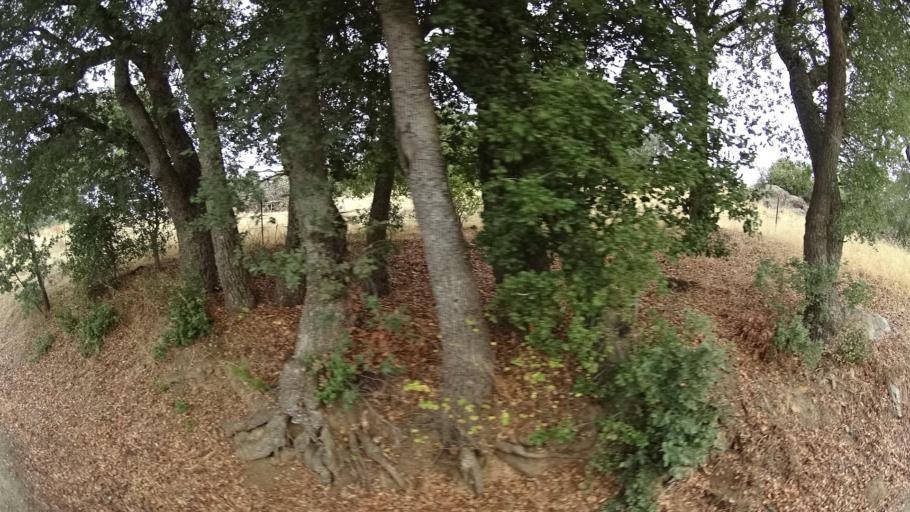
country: US
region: California
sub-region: San Diego County
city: Julian
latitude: 33.0435
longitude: -116.6402
